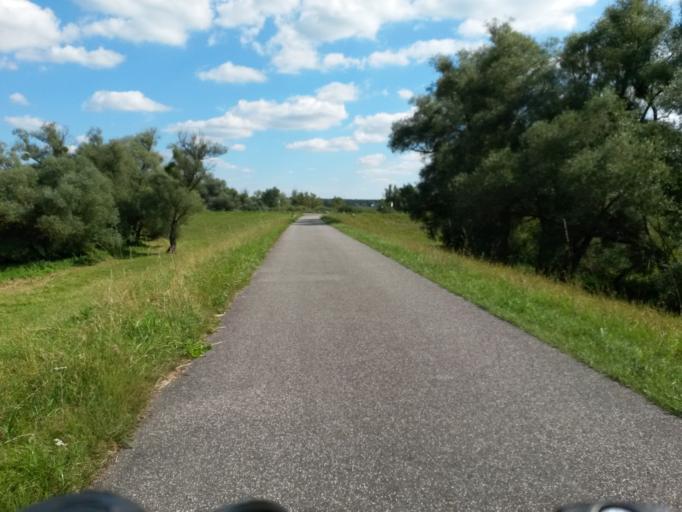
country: DE
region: Brandenburg
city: Schoneberg
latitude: 52.9876
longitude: 14.1759
